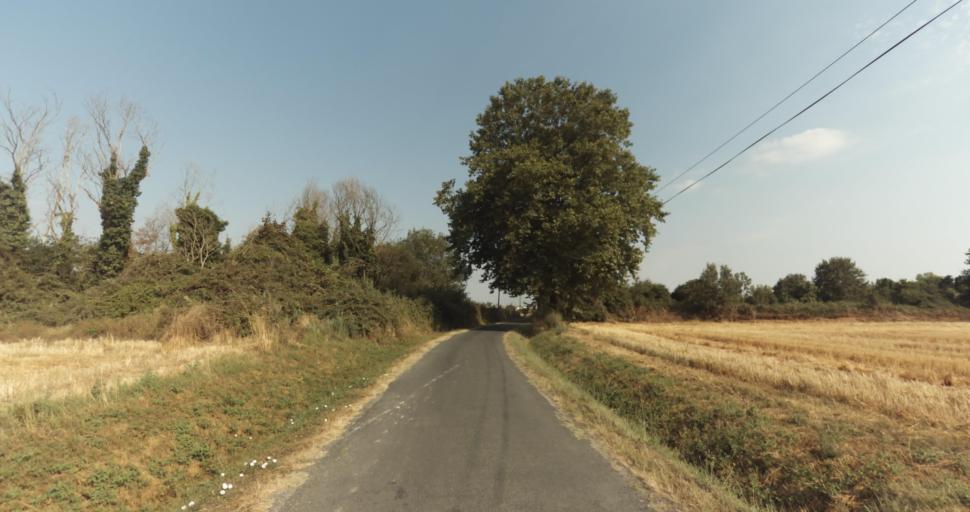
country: FR
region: Languedoc-Roussillon
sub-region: Departement des Pyrenees-Orientales
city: Latour-Bas-Elne
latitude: 42.6093
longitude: 3.0200
